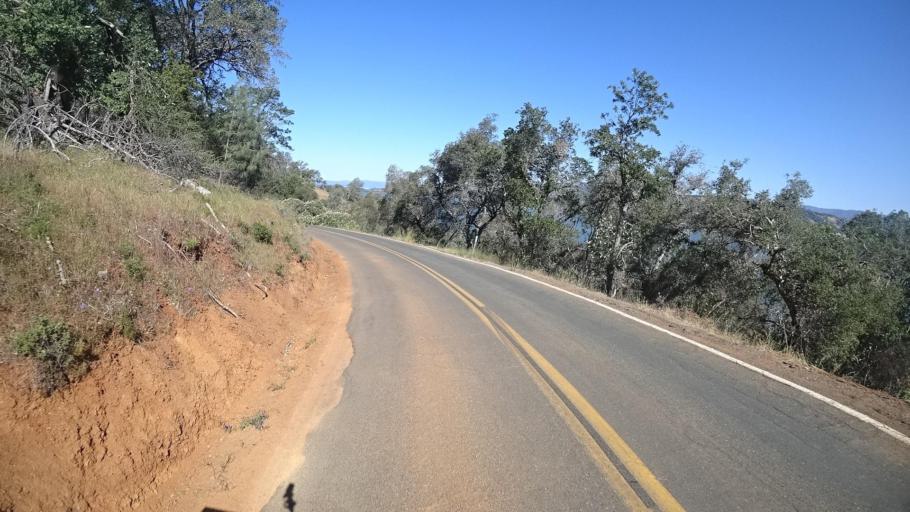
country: US
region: California
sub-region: Lake County
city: Clearlake Oaks
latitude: 38.9961
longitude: -122.6843
